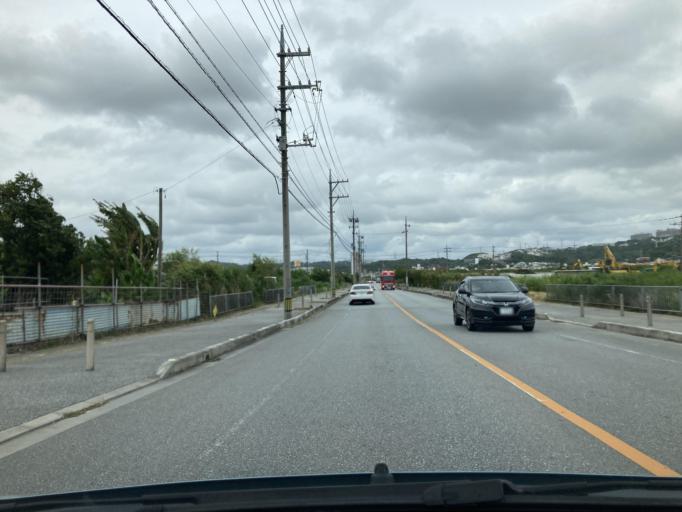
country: JP
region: Okinawa
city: Ginowan
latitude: 26.2207
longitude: 127.7750
